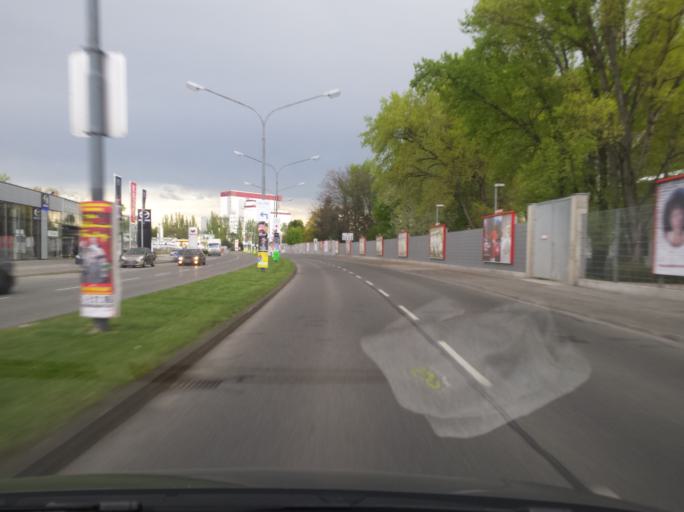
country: AT
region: Lower Austria
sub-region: Politischer Bezirk Wien-Umgebung
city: Gerasdorf bei Wien
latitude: 48.2297
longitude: 16.4436
